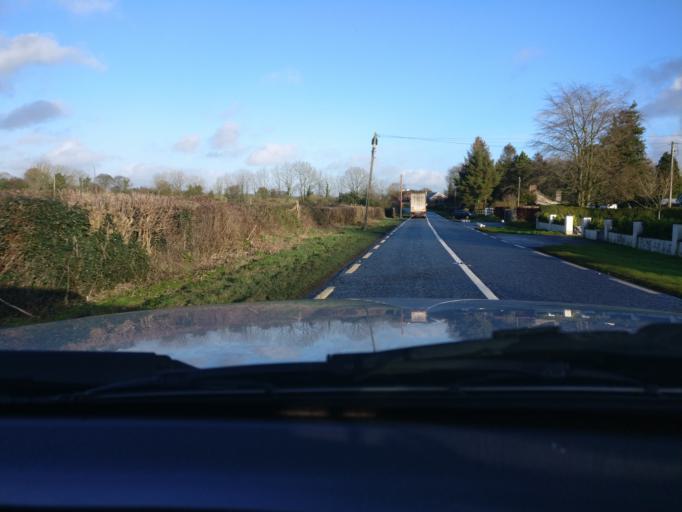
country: IE
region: Leinster
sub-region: An Iarmhi
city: Rathwire
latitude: 53.6245
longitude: -7.0776
